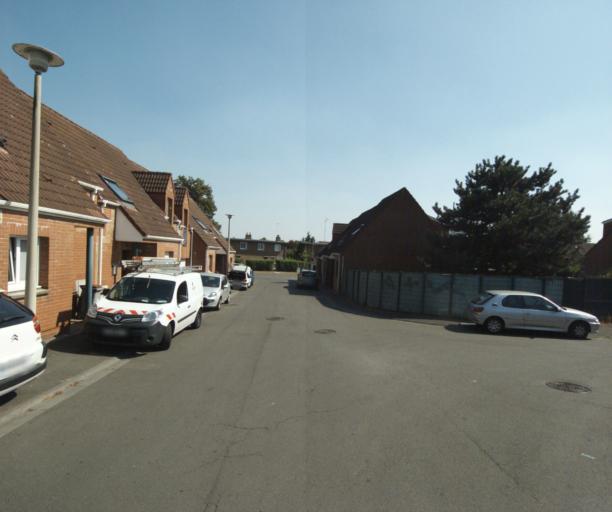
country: FR
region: Nord-Pas-de-Calais
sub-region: Departement du Nord
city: Roubaix
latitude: 50.7094
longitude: 3.1817
